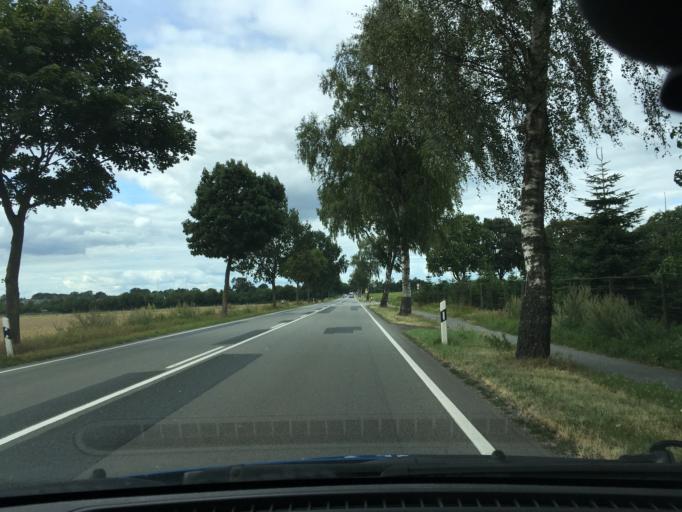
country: DE
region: Lower Saxony
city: Appel
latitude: 53.4139
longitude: 9.7893
